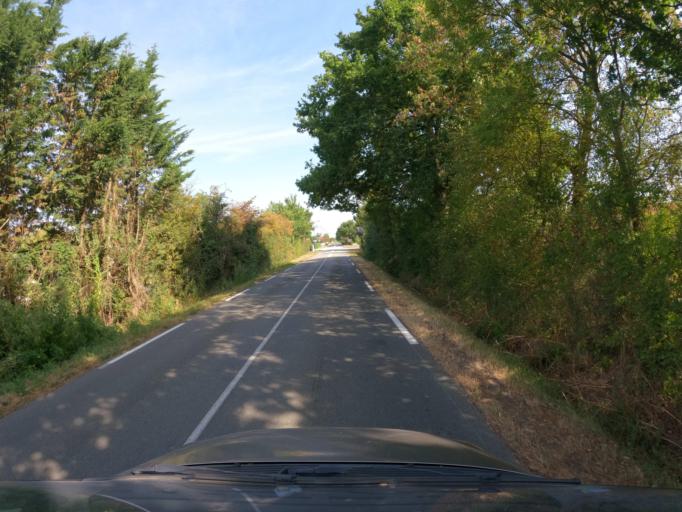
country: FR
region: Pays de la Loire
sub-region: Departement de la Vendee
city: Falleron
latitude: 46.8763
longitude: -1.7034
